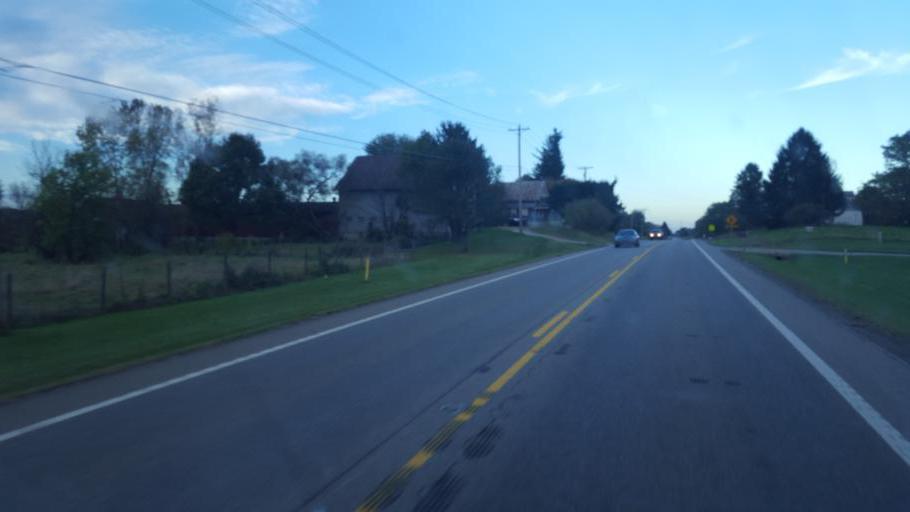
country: US
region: Ohio
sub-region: Licking County
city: Johnstown
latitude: 40.1869
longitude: -82.6134
